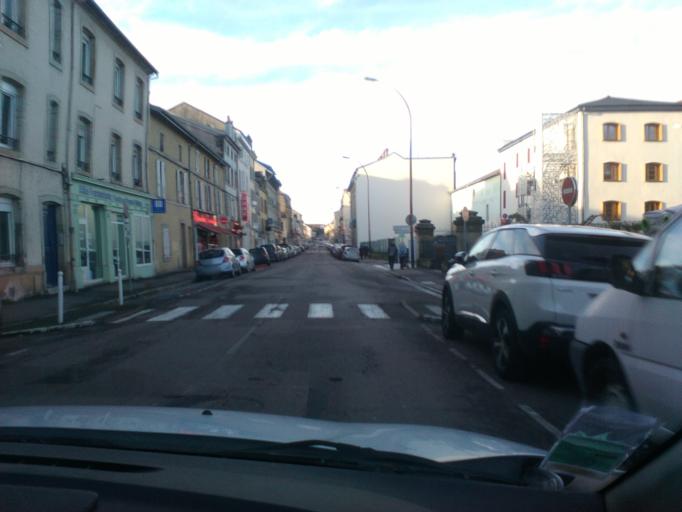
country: FR
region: Lorraine
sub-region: Departement des Vosges
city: Epinal
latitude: 48.1802
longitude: 6.4453
